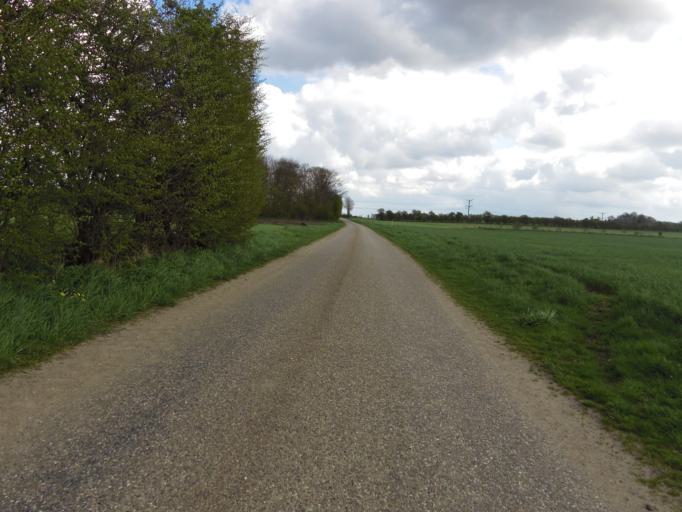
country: DK
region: South Denmark
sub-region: Tonder Kommune
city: Toftlund
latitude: 55.2153
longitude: 9.1359
